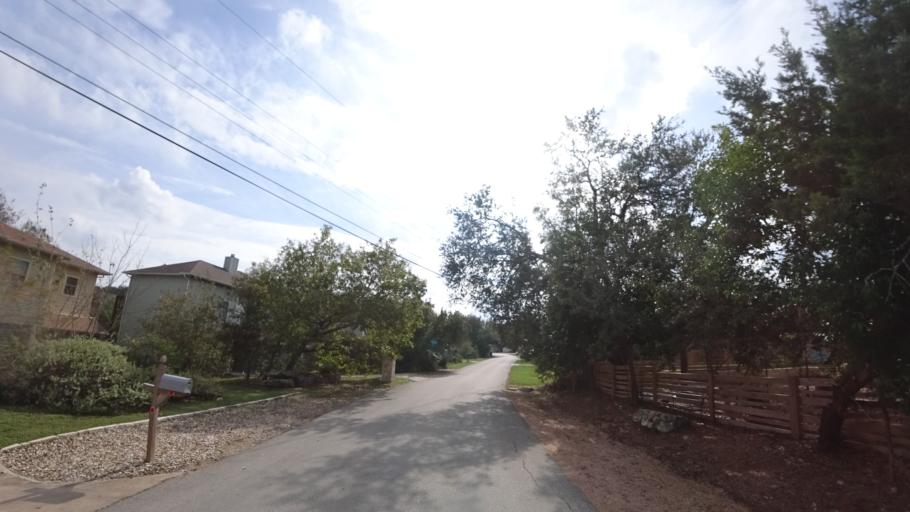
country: US
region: Texas
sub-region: Travis County
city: Hudson Bend
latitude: 30.3781
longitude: -97.9284
